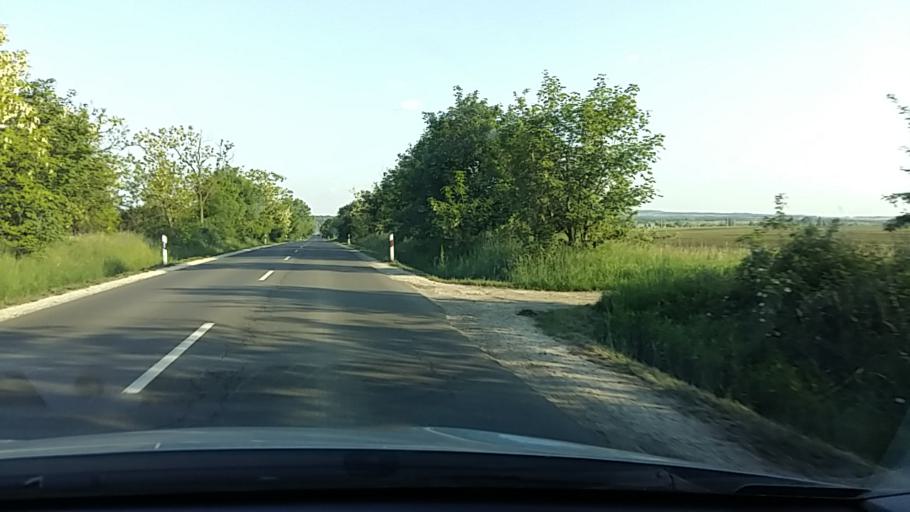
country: HU
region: Pest
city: Szod
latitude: 47.7292
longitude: 19.2251
